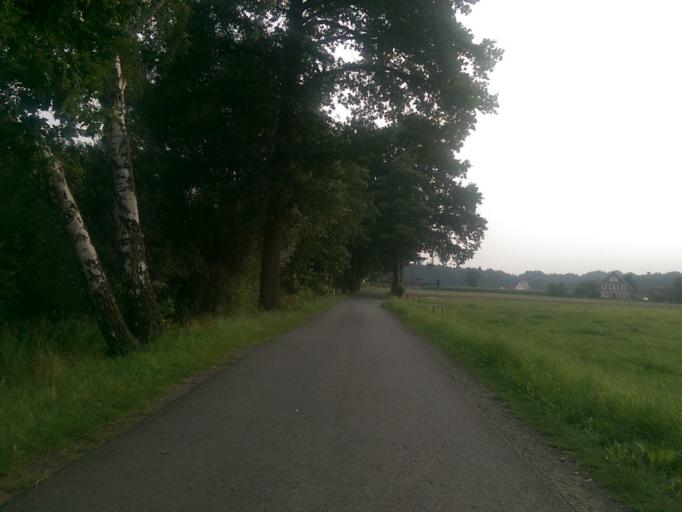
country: DE
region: North Rhine-Westphalia
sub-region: Regierungsbezirk Detmold
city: Guetersloh
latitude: 51.8741
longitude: 8.3646
